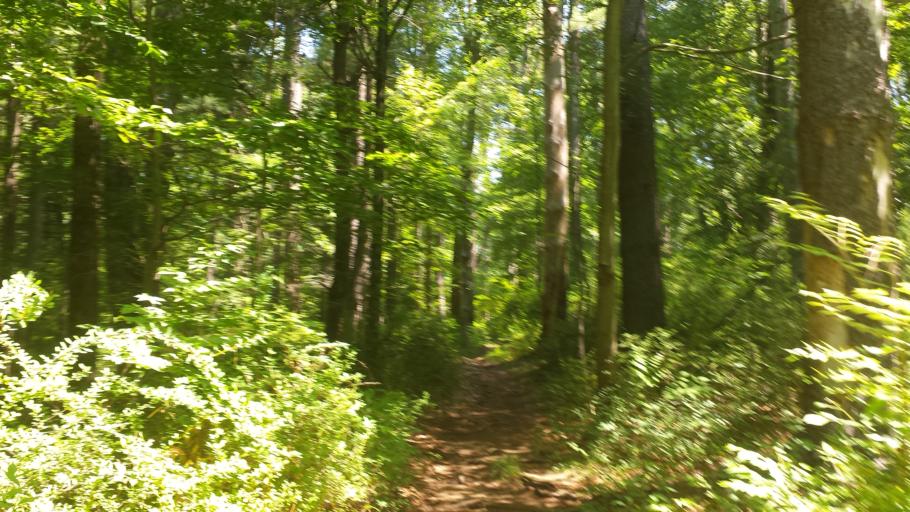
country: US
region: New York
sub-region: Westchester County
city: Pound Ridge
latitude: 41.2644
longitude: -73.5911
